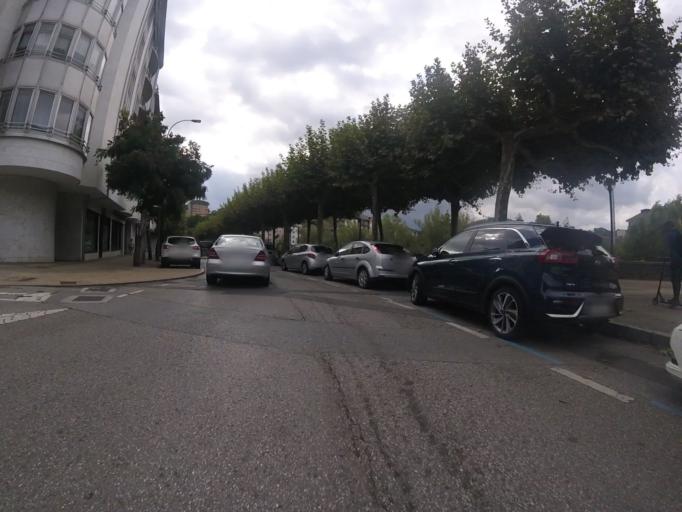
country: ES
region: Basque Country
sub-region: Provincia de Guipuzcoa
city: Tolosa
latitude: 43.1338
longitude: -2.0784
